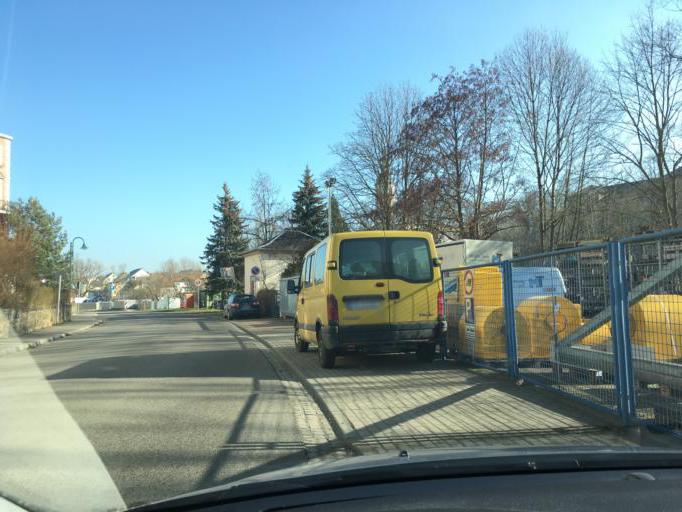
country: DE
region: Saxony
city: Penig
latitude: 50.9319
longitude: 12.6998
